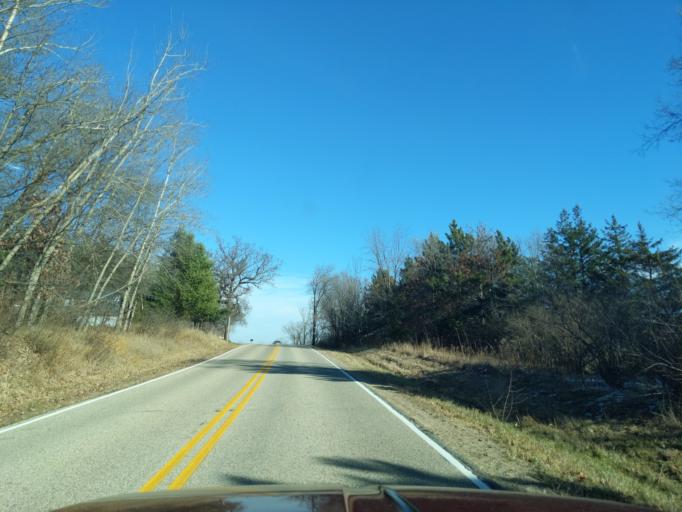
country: US
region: Wisconsin
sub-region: Waushara County
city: Silver Lake
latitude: 44.1153
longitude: -89.1771
